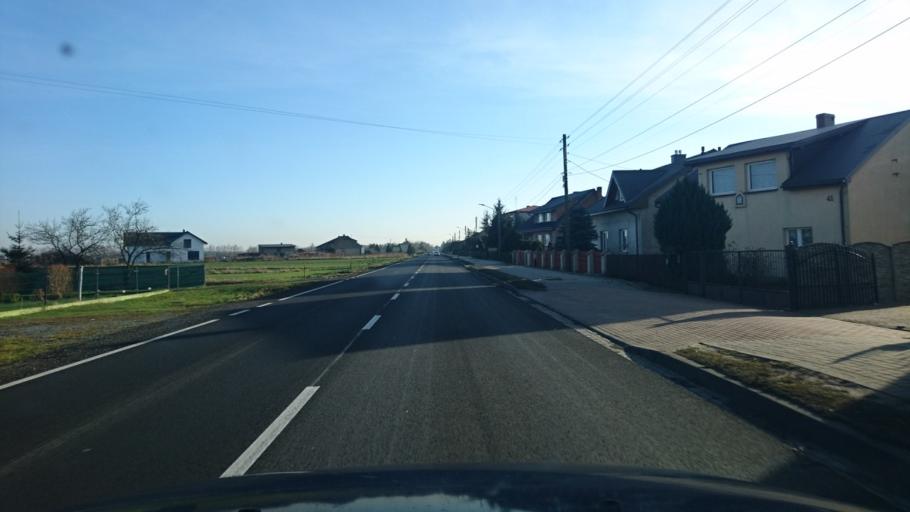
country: PL
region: Silesian Voivodeship
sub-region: Powiat klobucki
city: Starokrzepice
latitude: 51.0003
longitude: 18.6661
